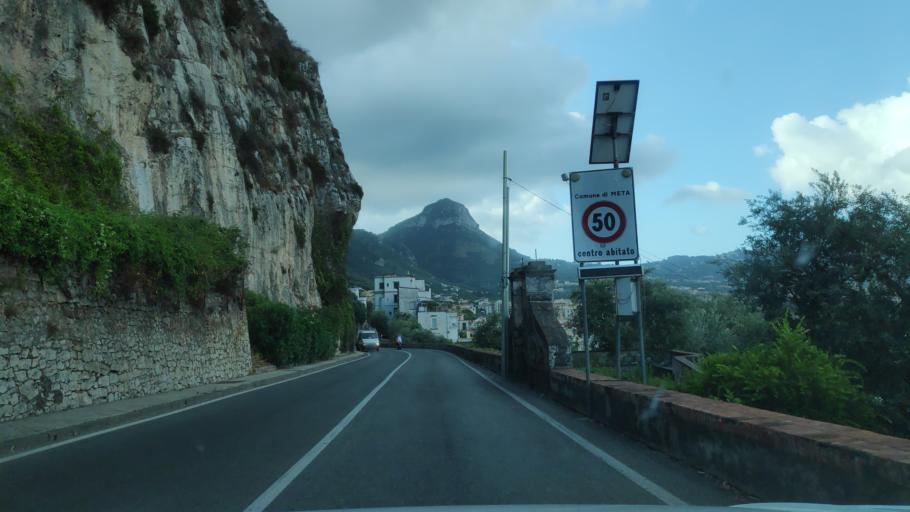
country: IT
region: Campania
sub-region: Provincia di Napoli
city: Meta
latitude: 40.6457
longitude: 14.4138
